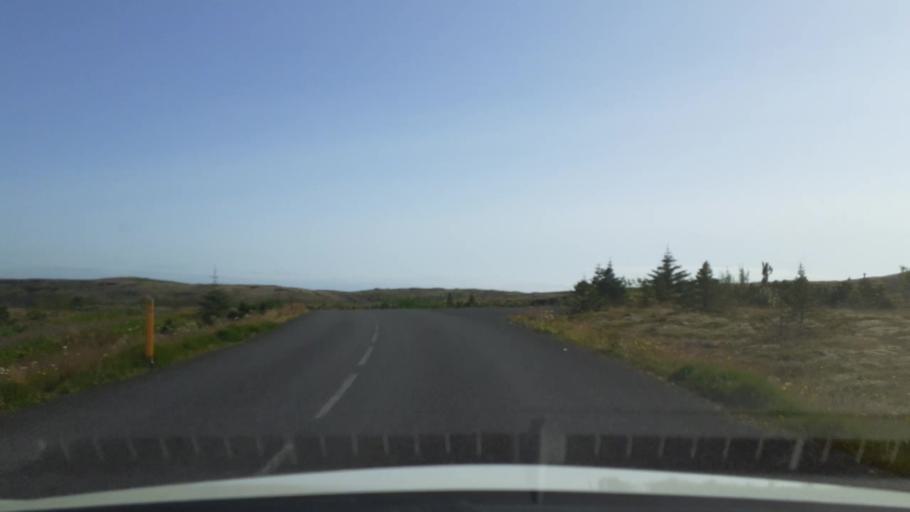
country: IS
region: South
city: Hveragerdi
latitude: 64.0161
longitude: -21.2105
